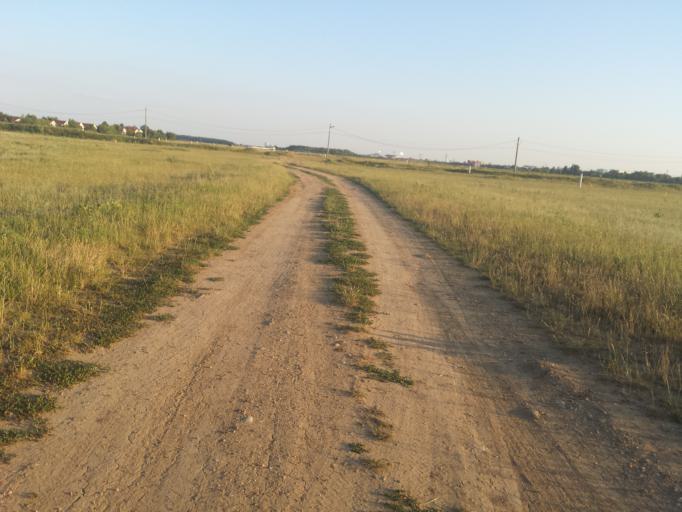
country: RO
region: Ilfov
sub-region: Voluntari City
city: Voluntari
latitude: 44.5162
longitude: 26.1527
